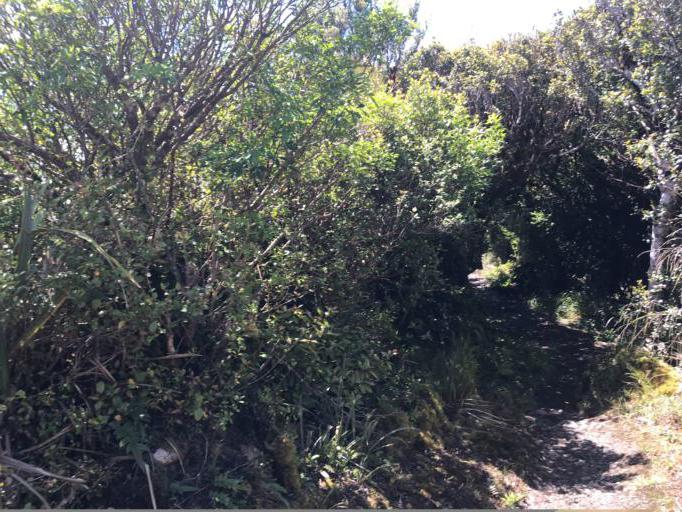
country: NZ
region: Wellington
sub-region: Kapiti Coast District
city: Otaki
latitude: -40.9088
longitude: 175.2577
